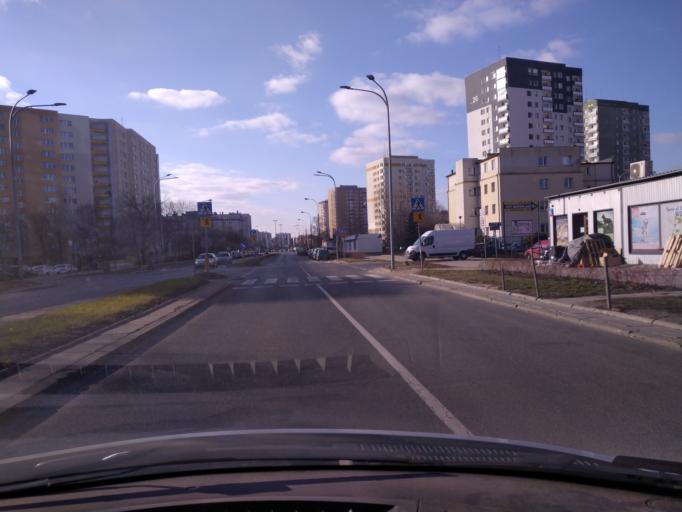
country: PL
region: Masovian Voivodeship
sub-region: Warszawa
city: Praga Poludnie
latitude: 52.2268
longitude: 21.0981
